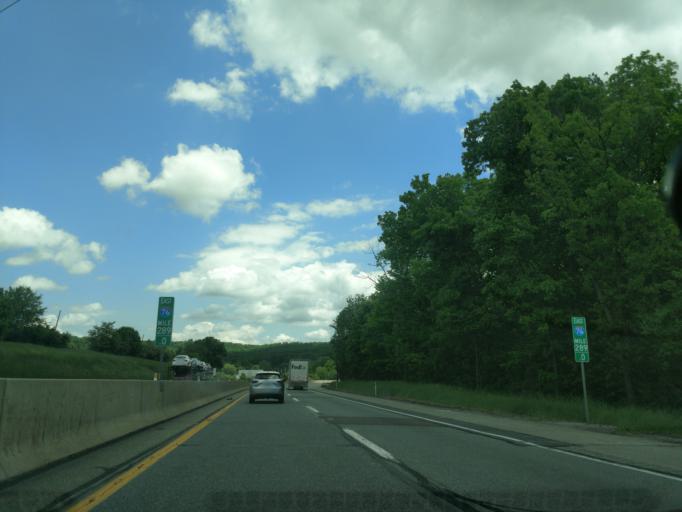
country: US
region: Pennsylvania
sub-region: Lancaster County
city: Bowmansville
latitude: 40.2097
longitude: -76.0287
